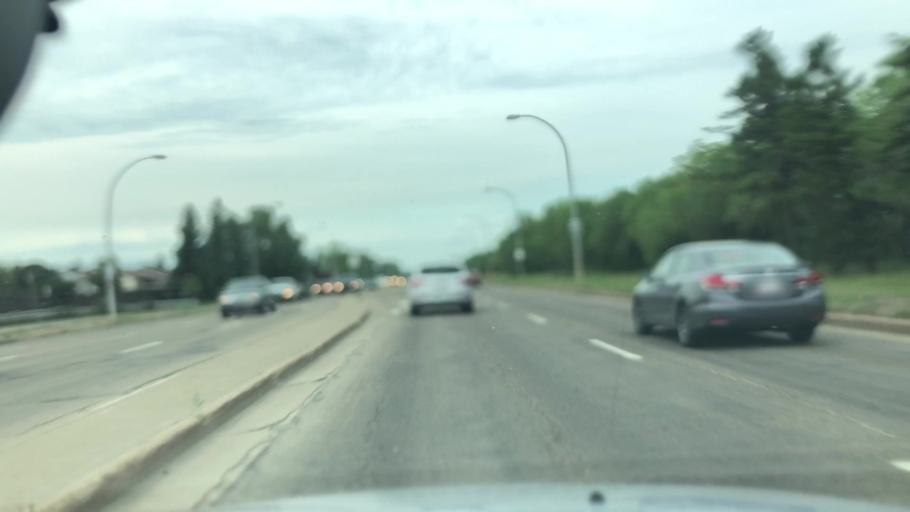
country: CA
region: Alberta
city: Edmonton
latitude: 53.6004
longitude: -113.5167
